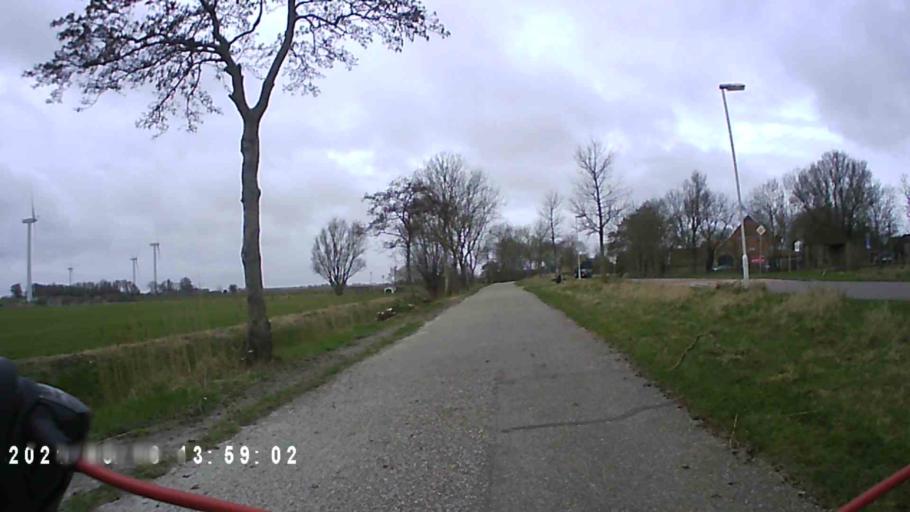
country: NL
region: Friesland
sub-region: Gemeente Franekeradeel
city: Sexbierum
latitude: 53.1837
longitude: 5.4989
